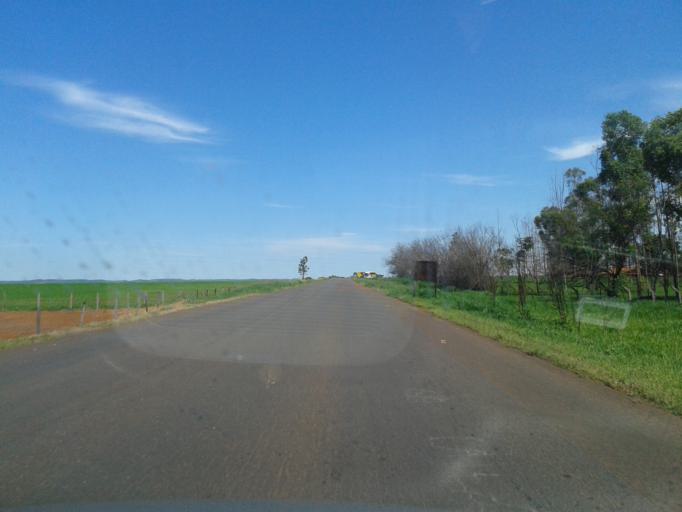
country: BR
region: Goias
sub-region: Piracanjuba
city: Piracanjuba
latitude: -17.1960
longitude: -48.7145
